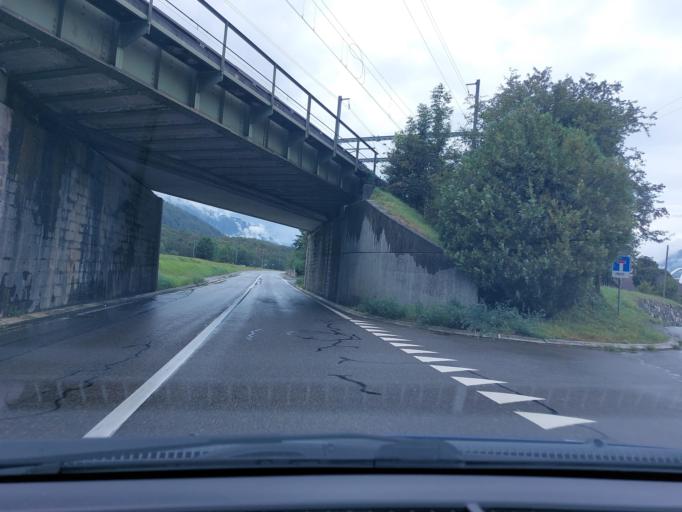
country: CH
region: Valais
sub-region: Saint-Maurice District
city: Saint-Maurice
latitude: 46.2314
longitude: 6.9994
